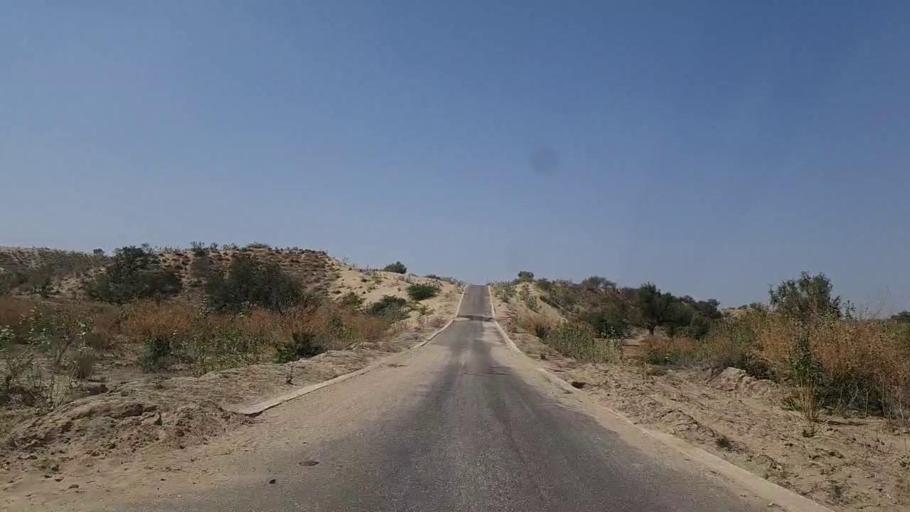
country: PK
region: Sindh
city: Diplo
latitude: 24.5756
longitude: 69.4864
